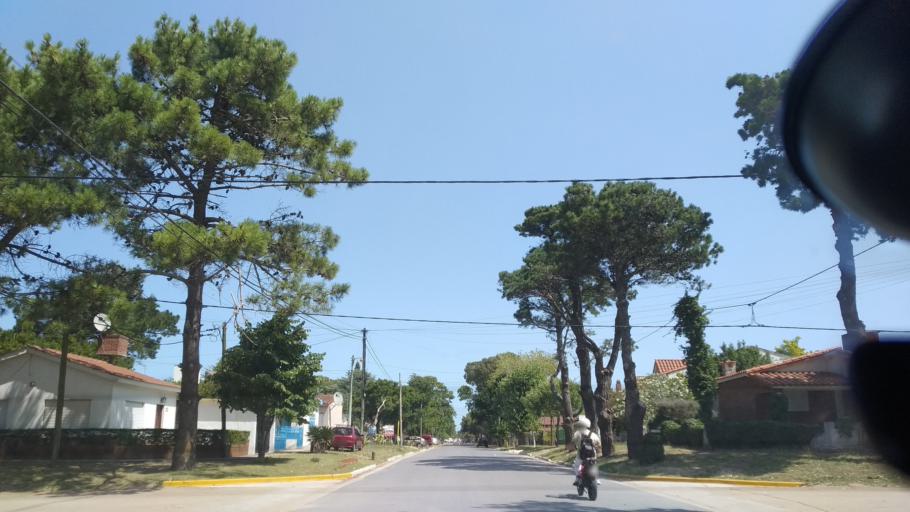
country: AR
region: Buenos Aires
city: Mar del Tuyu
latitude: -36.5762
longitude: -56.6938
